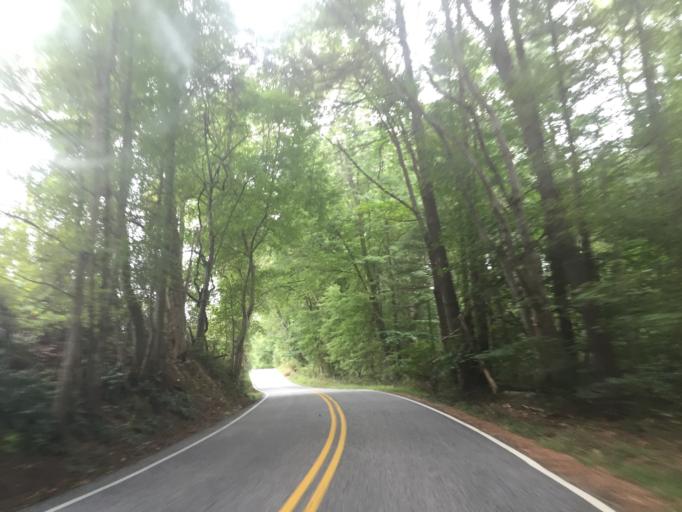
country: US
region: Maryland
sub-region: Harford County
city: Pleasant Hills
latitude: 39.5015
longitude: -76.3655
